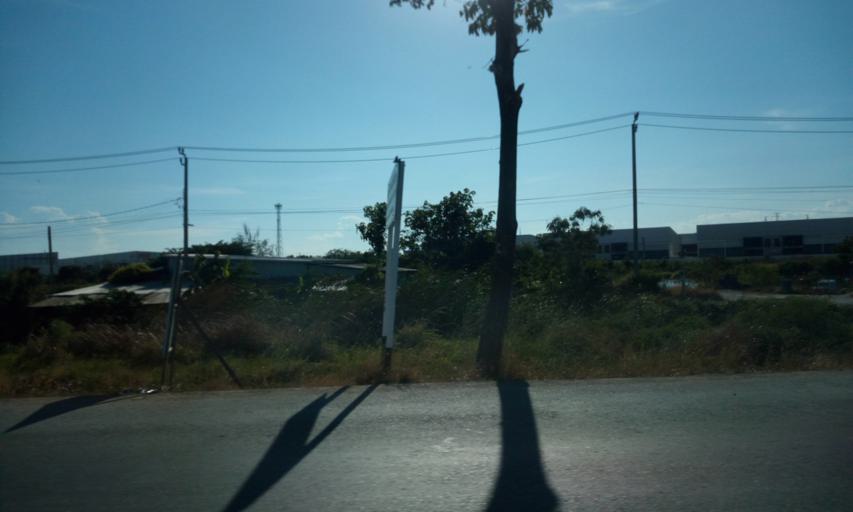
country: TH
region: Samut Prakan
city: Bang Bo District
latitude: 13.5791
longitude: 100.7577
